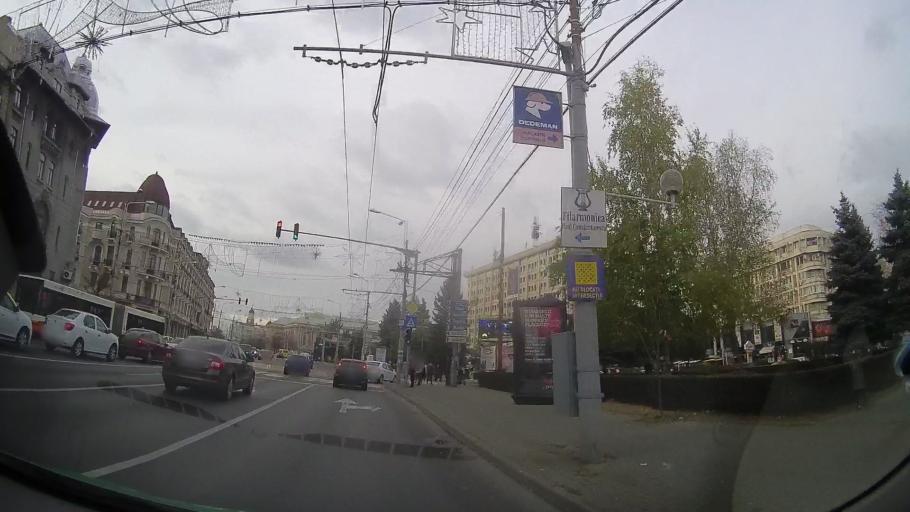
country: RO
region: Prahova
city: Ploiesti
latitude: 44.9401
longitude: 26.0242
